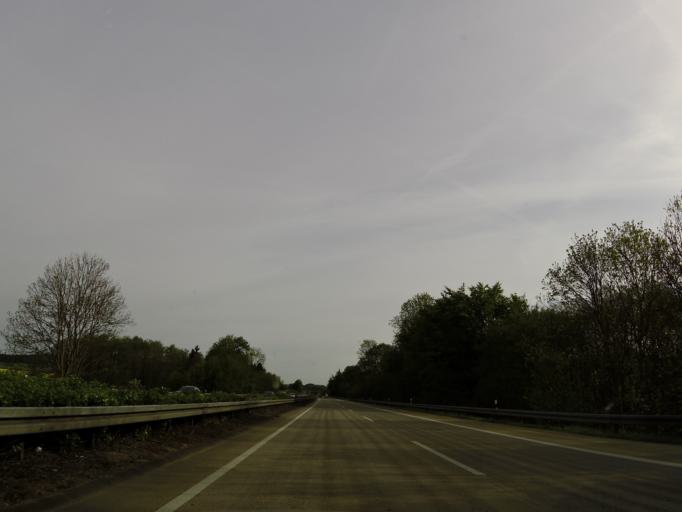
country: DE
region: Lower Saxony
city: Gittelde
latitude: 51.8377
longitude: 10.1183
